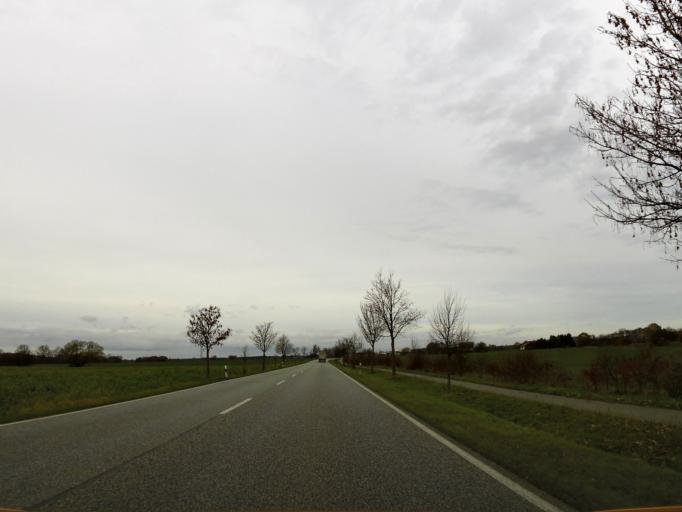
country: DE
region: Saxony-Anhalt
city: Pretzier
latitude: 52.8072
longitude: 11.2233
